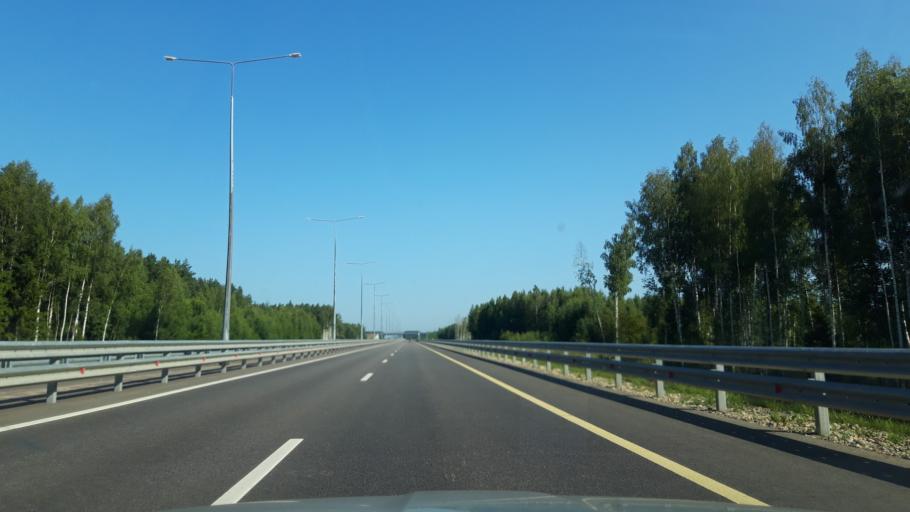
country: RU
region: Tverskaya
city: Zavidovo
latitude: 56.5401
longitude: 36.4936
